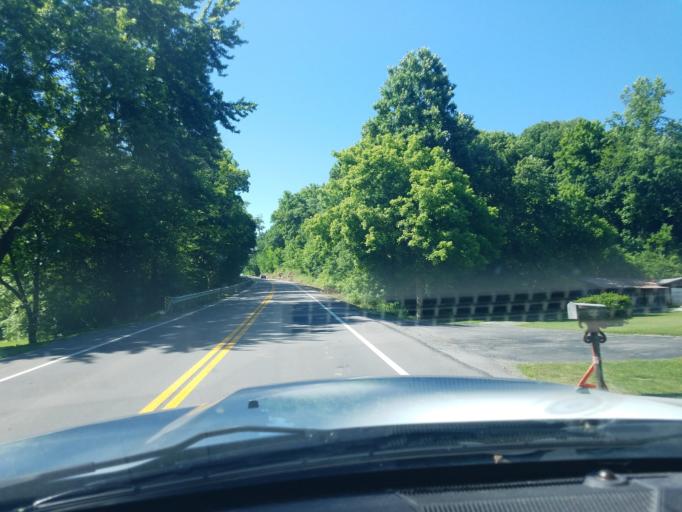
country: US
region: Tennessee
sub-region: Sumner County
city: Westmoreland
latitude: 36.4781
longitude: -86.2713
